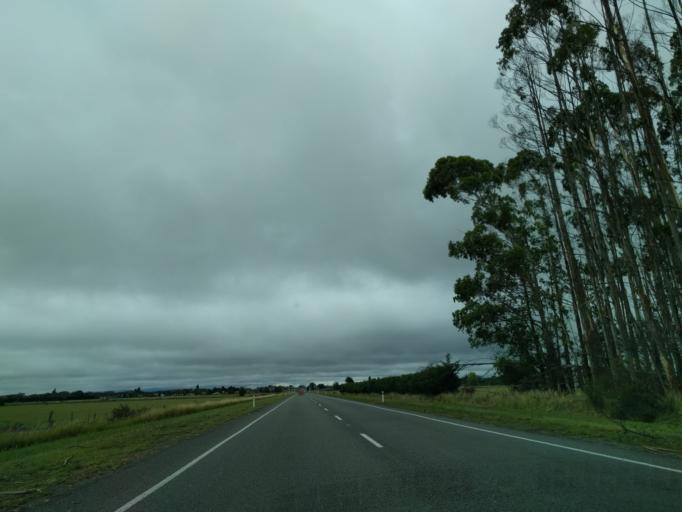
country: NZ
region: Canterbury
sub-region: Waimakariri District
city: Kaiapoi
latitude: -43.3646
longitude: 172.6512
